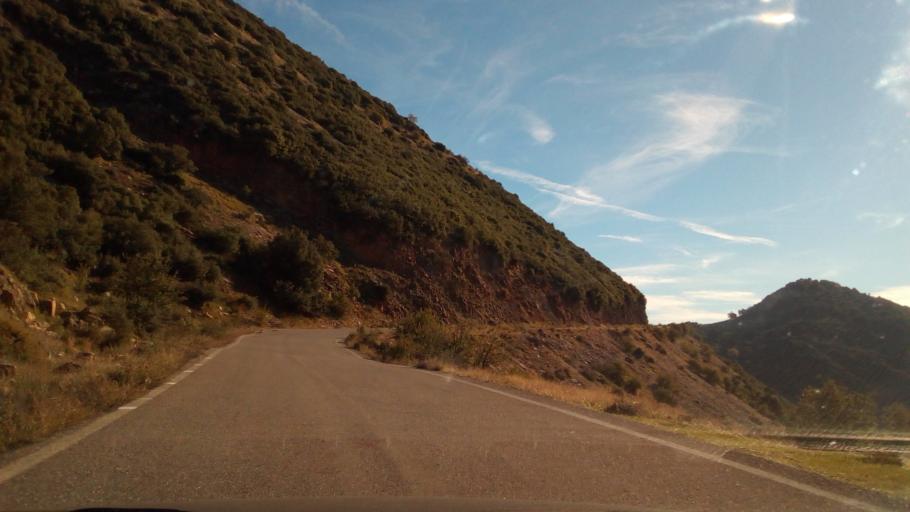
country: GR
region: West Greece
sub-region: Nomos Aitolias kai Akarnanias
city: Nafpaktos
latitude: 38.4842
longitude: 21.8613
